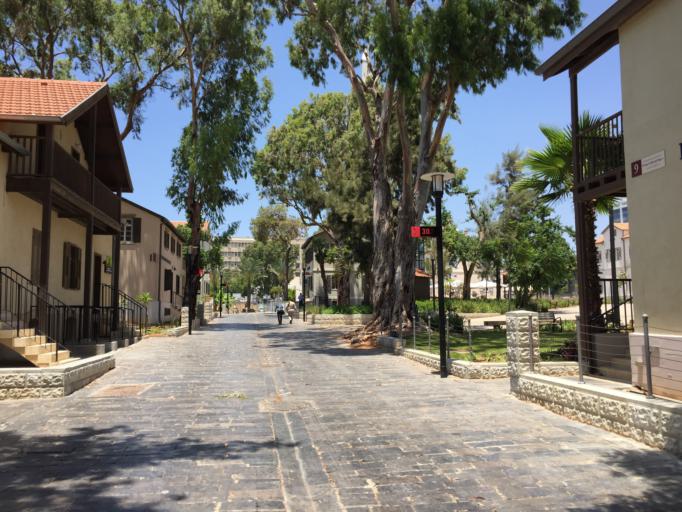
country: IL
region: Tel Aviv
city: Tel Aviv
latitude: 32.0724
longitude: 34.7871
